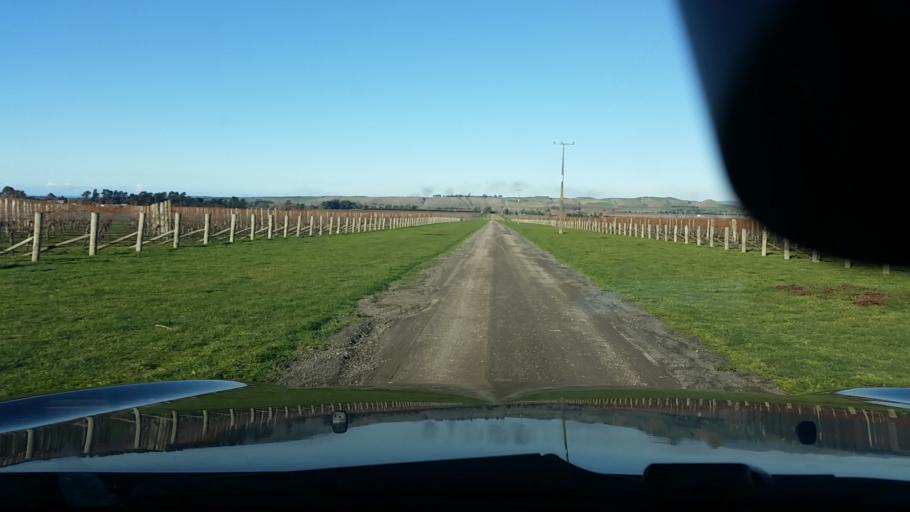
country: NZ
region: Marlborough
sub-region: Marlborough District
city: Blenheim
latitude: -41.6395
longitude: 174.0347
